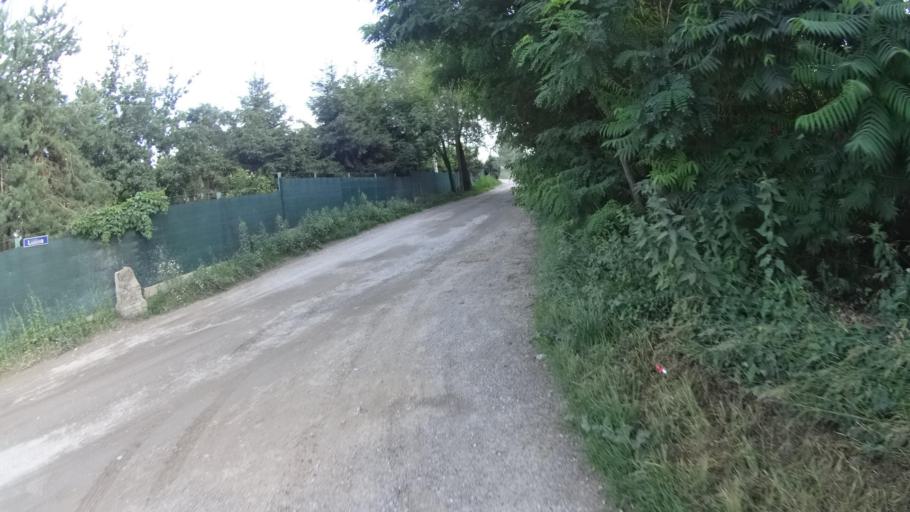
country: PL
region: Masovian Voivodeship
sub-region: Powiat piaseczynski
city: Tarczyn
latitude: 51.9764
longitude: 20.8536
